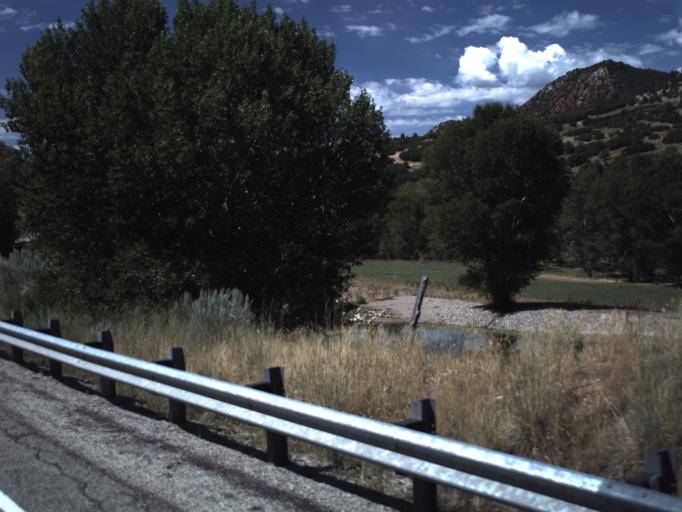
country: US
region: Utah
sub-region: Utah County
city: Woodland Hills
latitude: 39.9754
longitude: -111.5039
